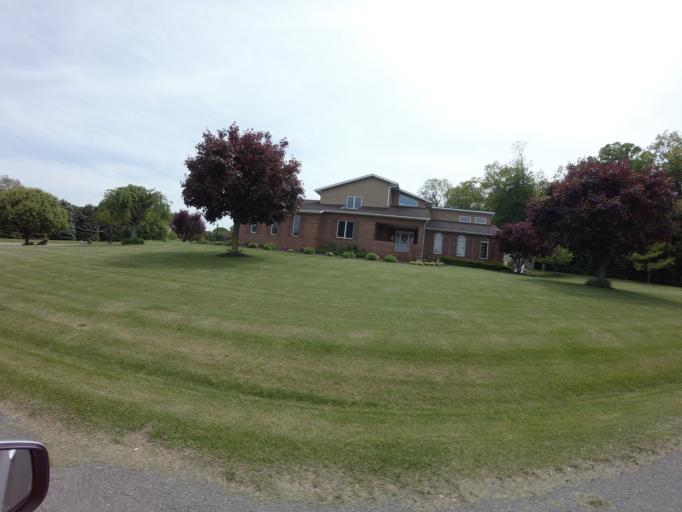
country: US
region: Maryland
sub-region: Carroll County
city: New Windsor
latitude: 39.4629
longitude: -77.0696
